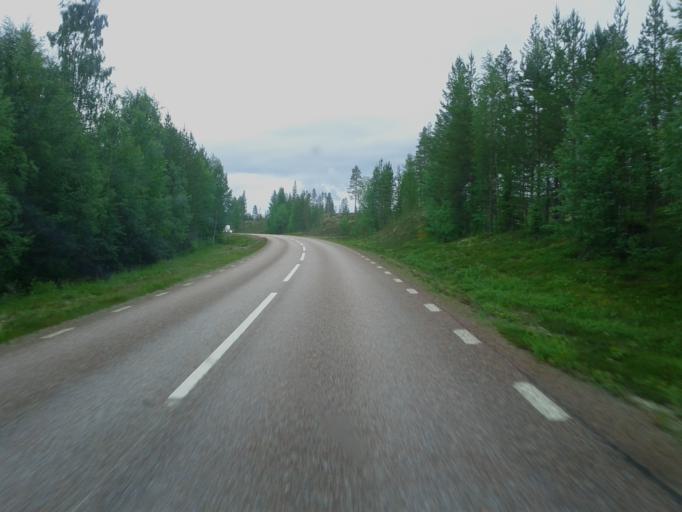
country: NO
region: Hedmark
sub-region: Trysil
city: Innbygda
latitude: 61.7197
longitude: 13.0000
